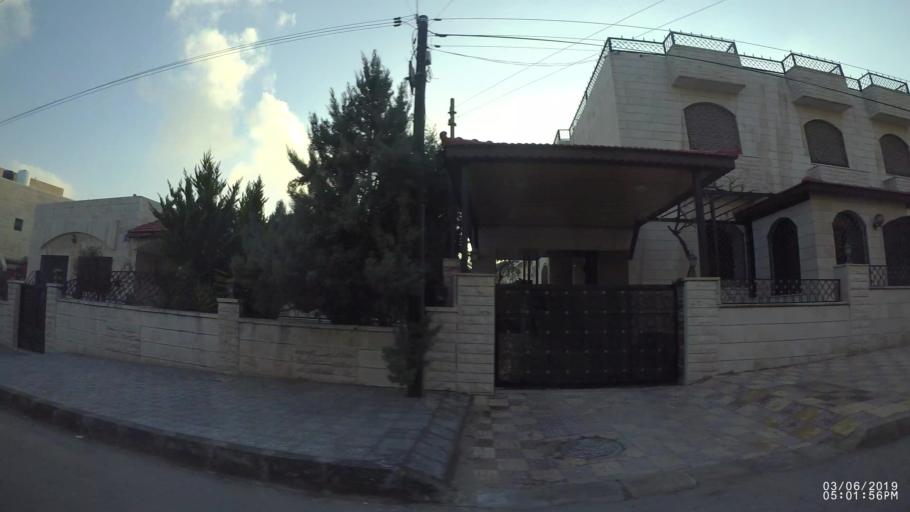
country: JO
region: Amman
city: Amman
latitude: 31.9962
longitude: 35.9523
